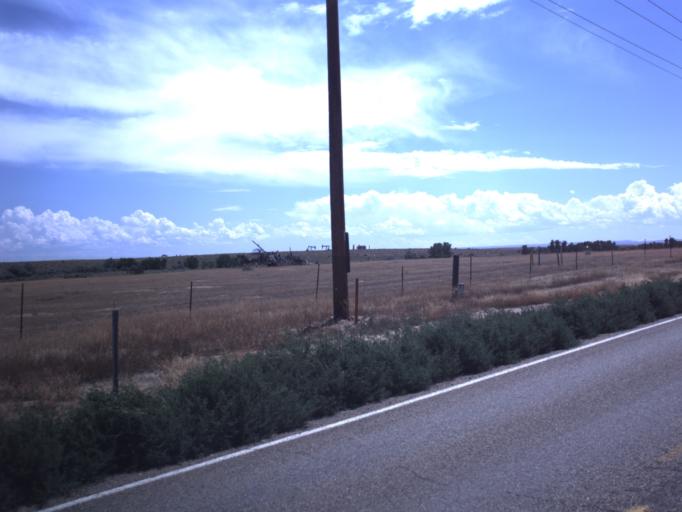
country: US
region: Utah
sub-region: Uintah County
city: Naples
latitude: 40.1493
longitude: -109.6641
